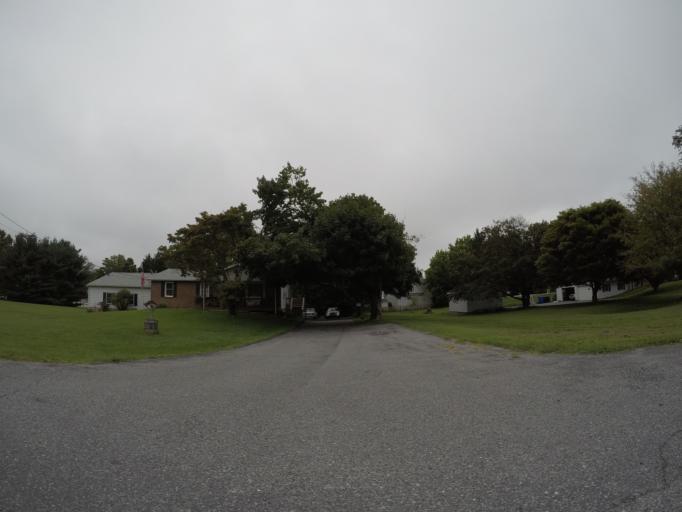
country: US
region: Maryland
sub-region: Carroll County
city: Sykesville
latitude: 39.3348
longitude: -77.0491
